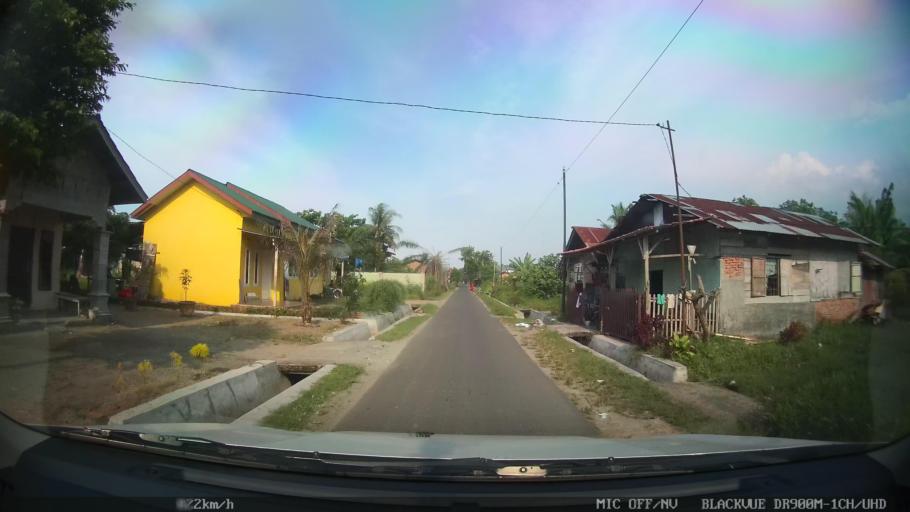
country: ID
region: North Sumatra
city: Binjai
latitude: 3.6029
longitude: 98.4972
